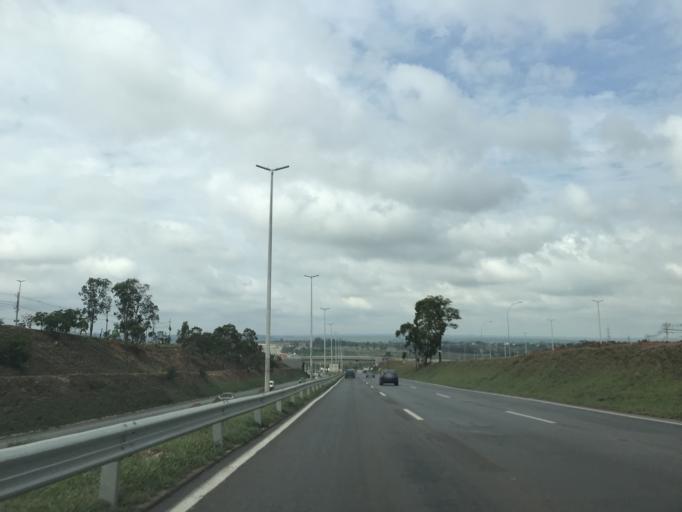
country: BR
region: Federal District
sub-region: Brasilia
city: Brasilia
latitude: -15.6986
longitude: -47.8803
